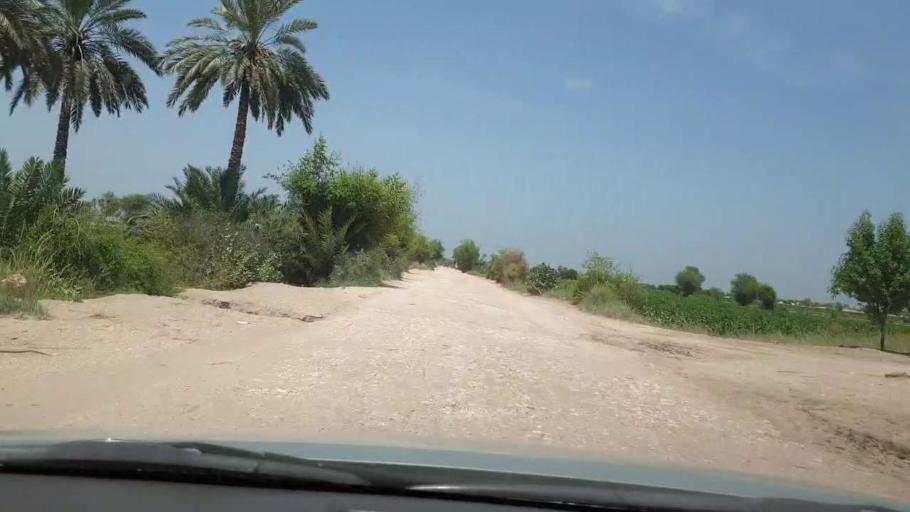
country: PK
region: Sindh
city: Pano Aqil
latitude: 27.6991
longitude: 69.2176
